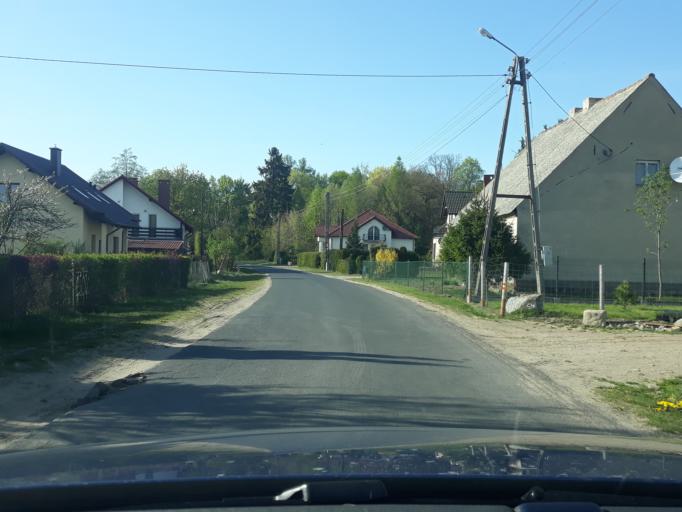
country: PL
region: Pomeranian Voivodeship
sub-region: Powiat czluchowski
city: Przechlewo
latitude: 53.8732
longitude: 17.3317
